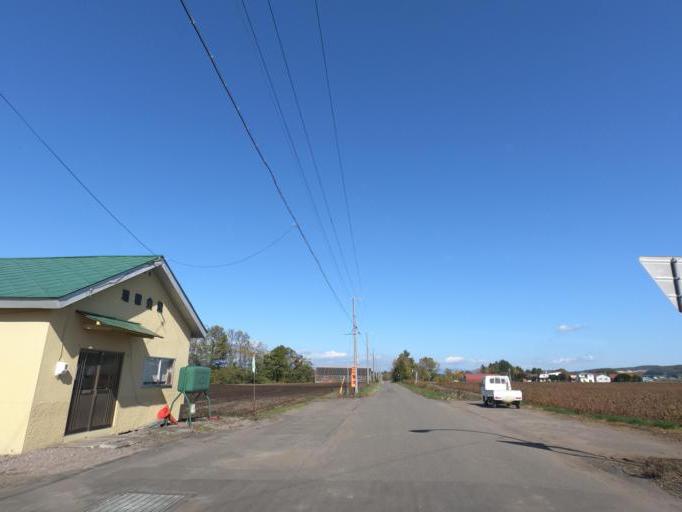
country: JP
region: Hokkaido
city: Otofuke
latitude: 43.0495
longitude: 143.2746
